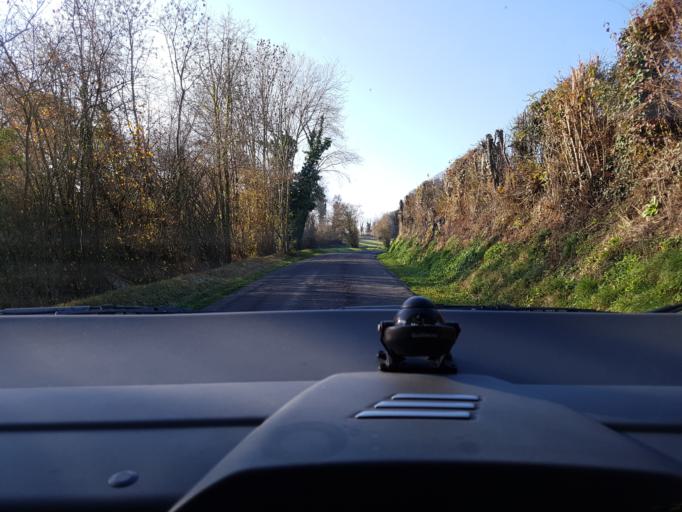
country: FR
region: Lower Normandy
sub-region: Departement du Calvados
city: Saint-Remy
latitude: 48.9396
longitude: -0.5357
